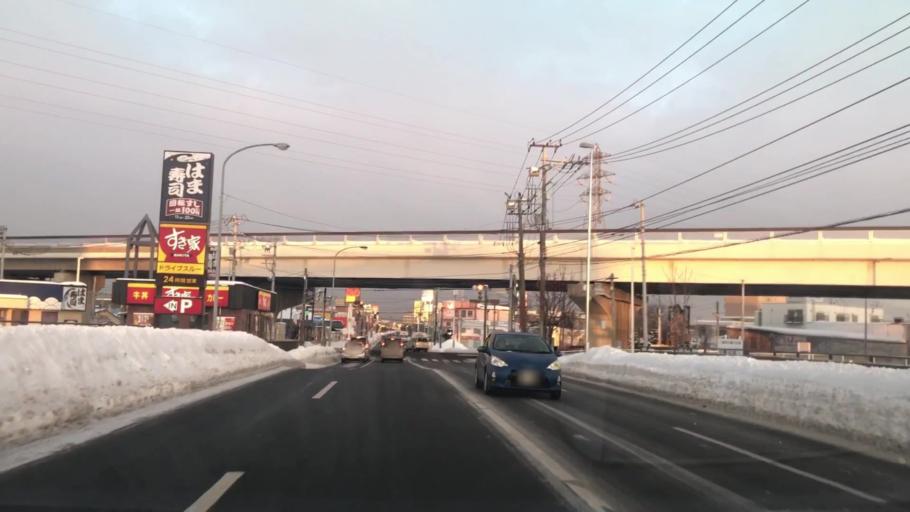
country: JP
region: Hokkaido
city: Sapporo
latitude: 43.0967
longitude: 141.2986
